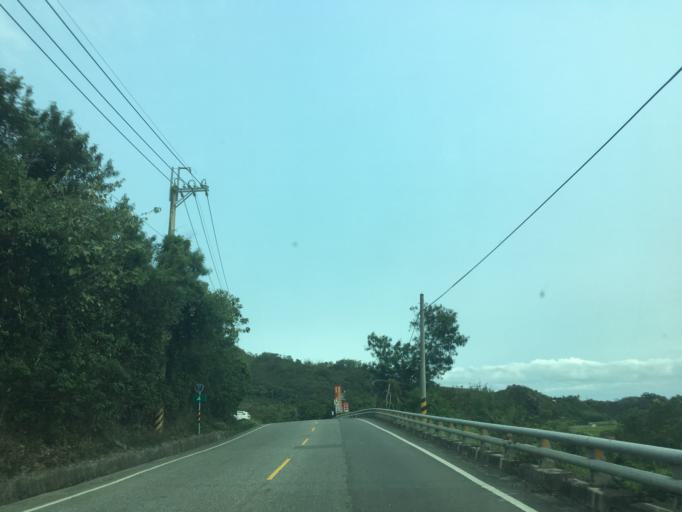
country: TW
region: Taiwan
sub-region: Taitung
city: Taitung
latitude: 22.7907
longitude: 121.1492
